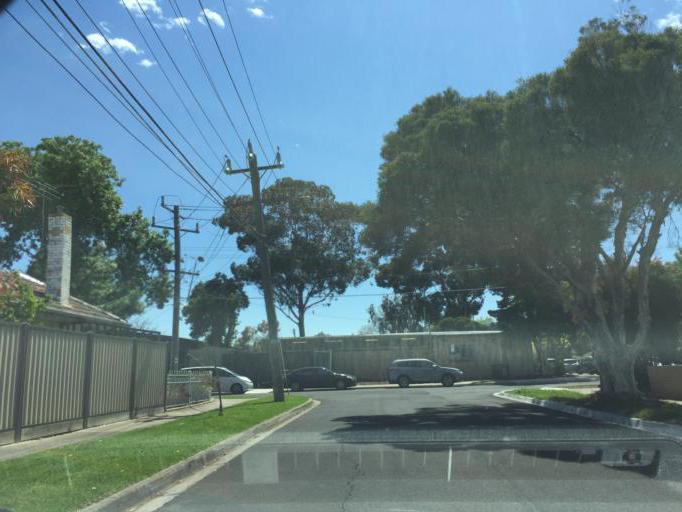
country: AU
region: Victoria
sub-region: Maribyrnong
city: Braybrook
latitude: -37.7881
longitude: 144.8446
